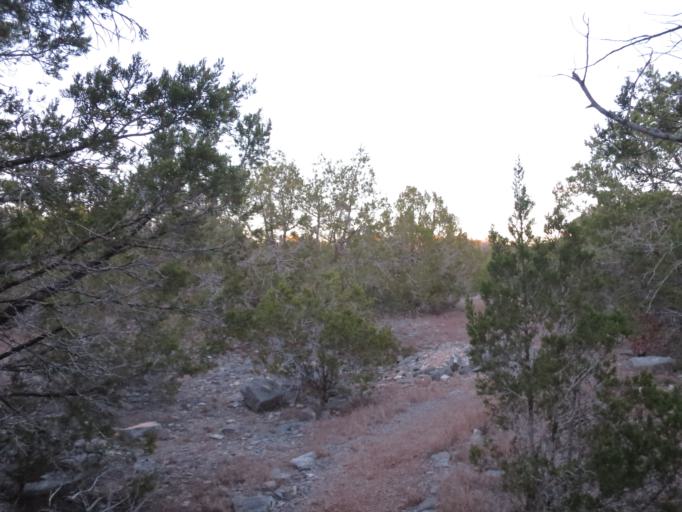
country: US
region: Texas
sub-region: Travis County
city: Lago Vista
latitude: 30.5054
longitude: -97.9872
